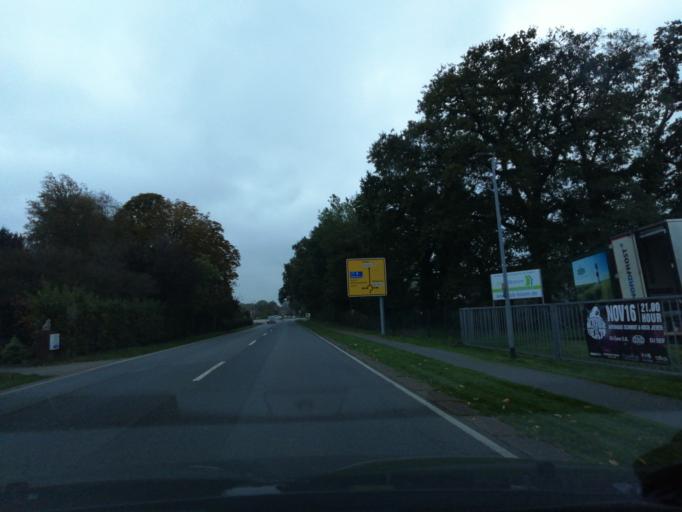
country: DE
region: Lower Saxony
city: Schortens
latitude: 53.5378
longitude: 7.9659
